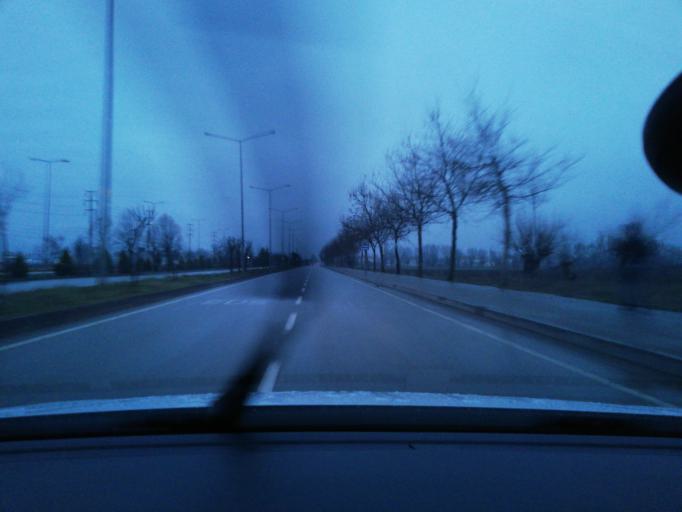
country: TR
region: Bolu
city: Bolu
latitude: 40.7187
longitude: 31.6139
